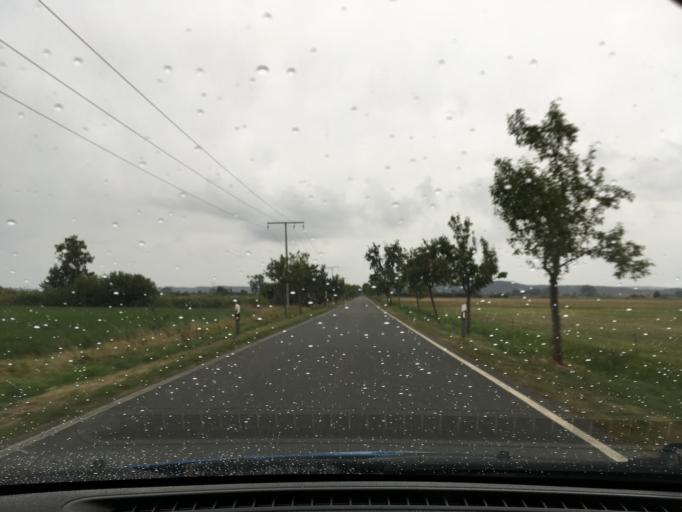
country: DE
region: Lower Saxony
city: Hitzacker
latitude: 53.2242
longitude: 10.9884
